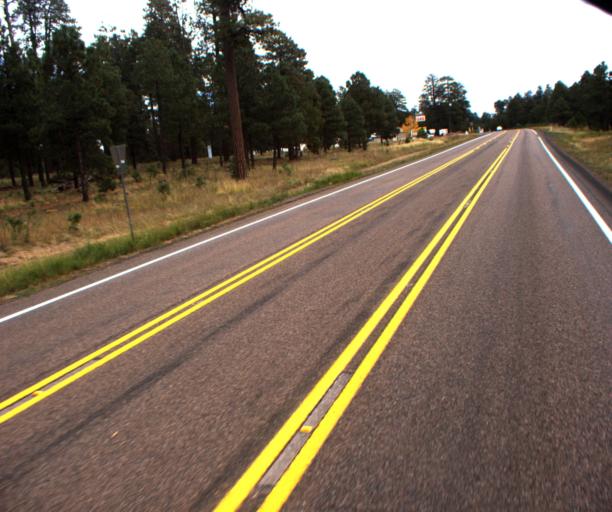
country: US
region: Arizona
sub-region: Navajo County
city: Heber-Overgaard
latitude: 34.3301
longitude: -110.7778
